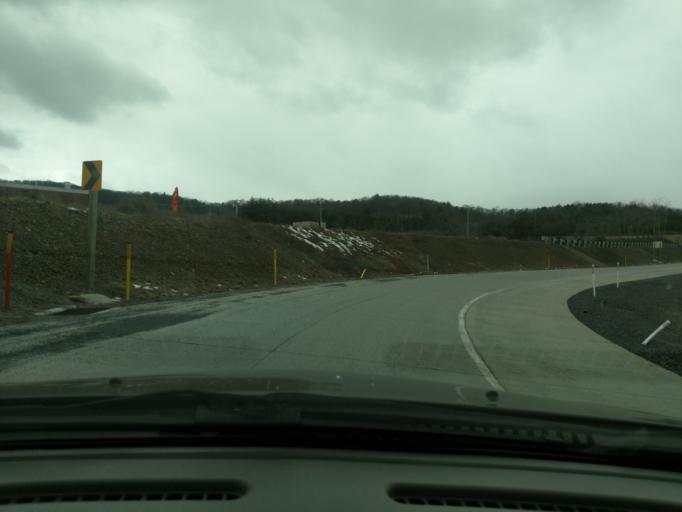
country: US
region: Pennsylvania
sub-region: Schuylkill County
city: Orwigsburg
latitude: 40.6288
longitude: -76.0641
